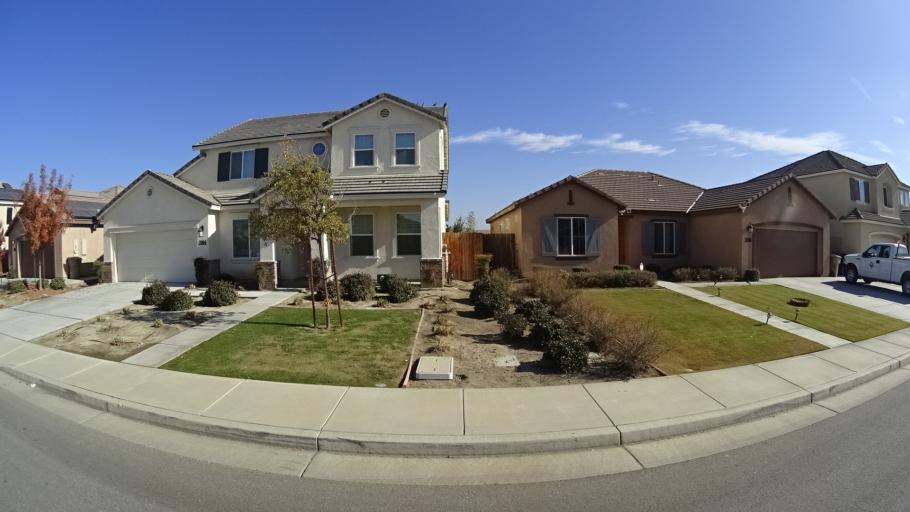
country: US
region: California
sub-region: Kern County
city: Greenfield
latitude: 35.2840
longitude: -119.0577
